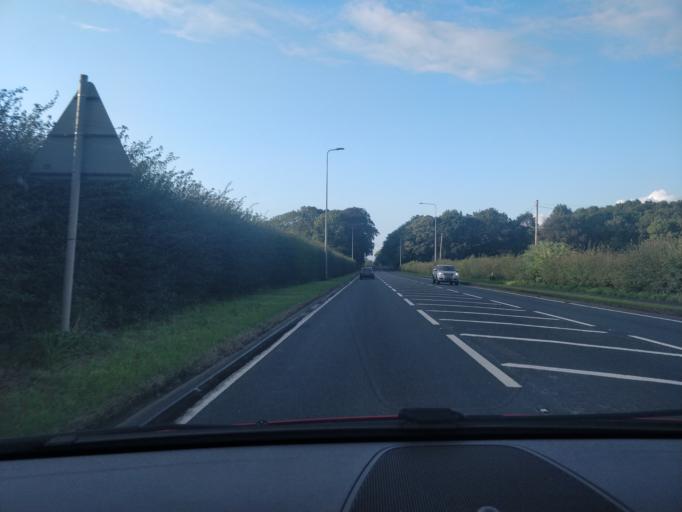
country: GB
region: England
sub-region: Lancashire
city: Tarleton
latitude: 53.6783
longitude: -2.8174
